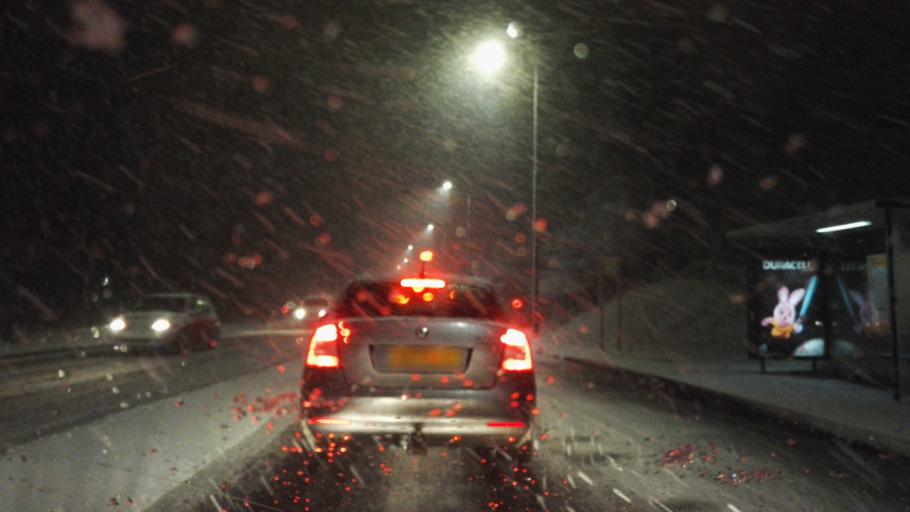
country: NL
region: Gelderland
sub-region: Gemeente Apeldoorn
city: Apeldoorn
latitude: 52.2180
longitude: 6.0018
